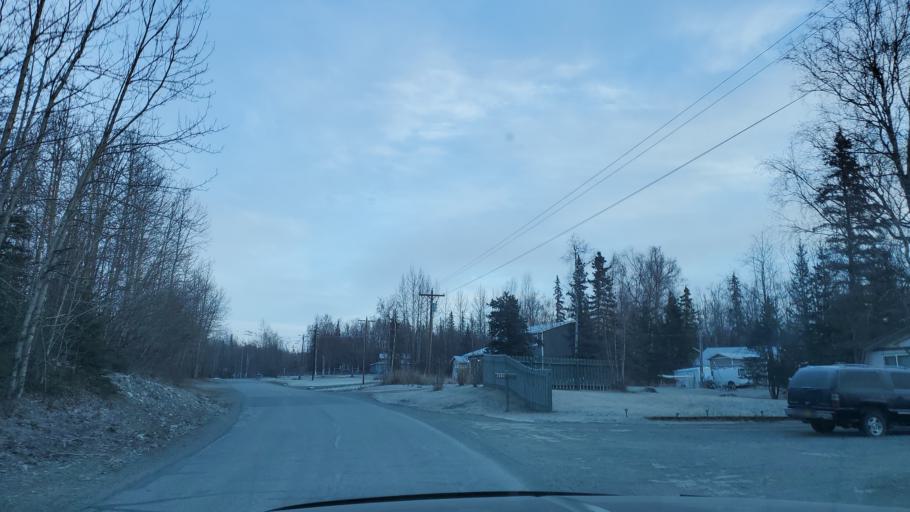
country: US
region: Alaska
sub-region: Matanuska-Susitna Borough
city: Lakes
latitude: 61.6087
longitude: -149.3112
